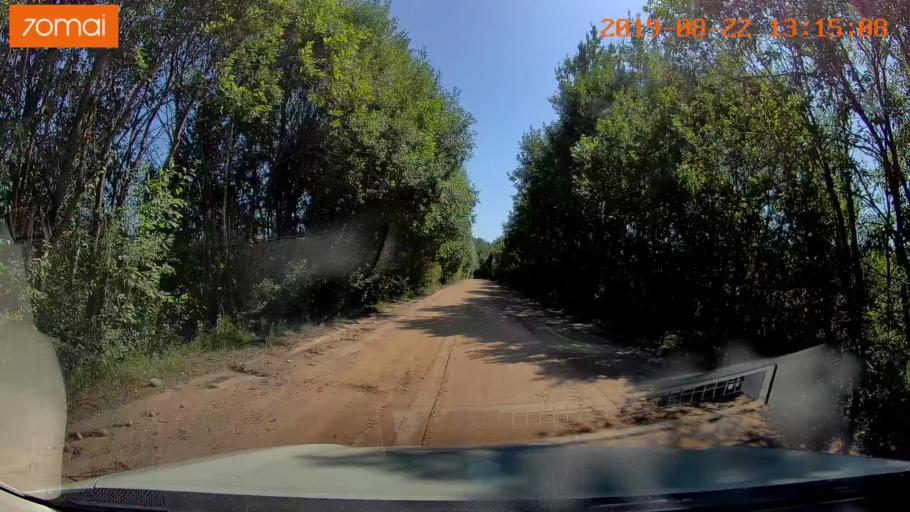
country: BY
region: Minsk
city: Prawdzinski
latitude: 53.2623
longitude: 27.8934
